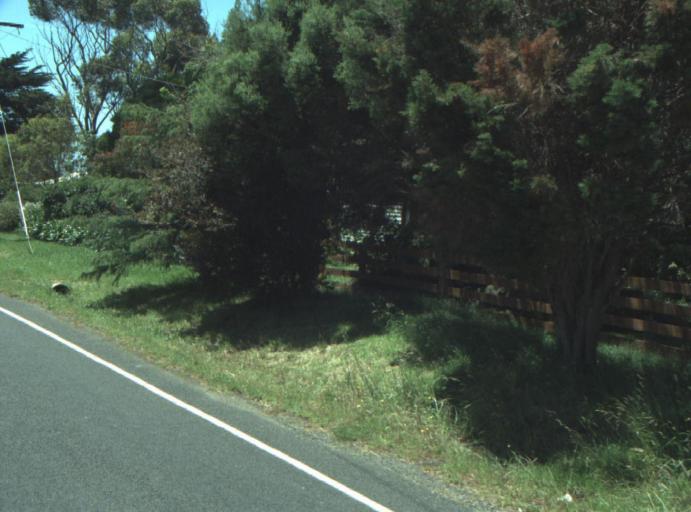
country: AU
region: Victoria
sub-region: Greater Geelong
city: Clifton Springs
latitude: -38.2509
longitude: 144.5652
